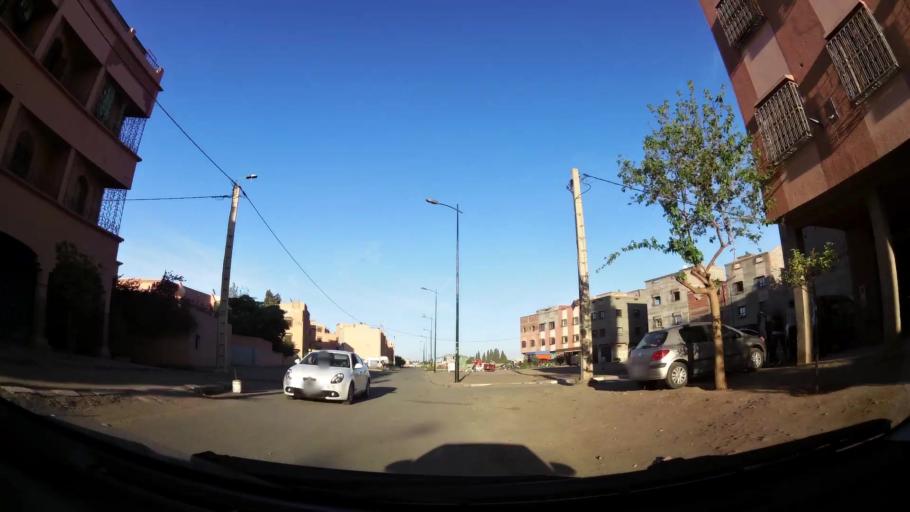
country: MA
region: Marrakech-Tensift-Al Haouz
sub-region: Marrakech
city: Marrakesh
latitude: 31.6175
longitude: -8.0478
